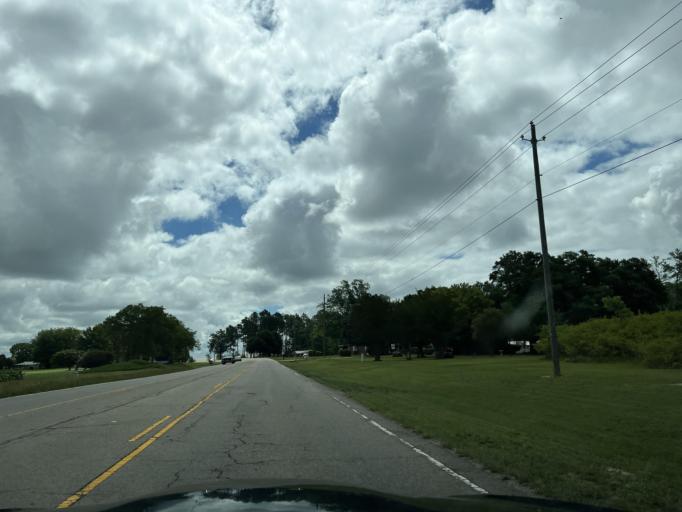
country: US
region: North Carolina
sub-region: Lee County
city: Sanford
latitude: 35.4372
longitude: -79.1945
